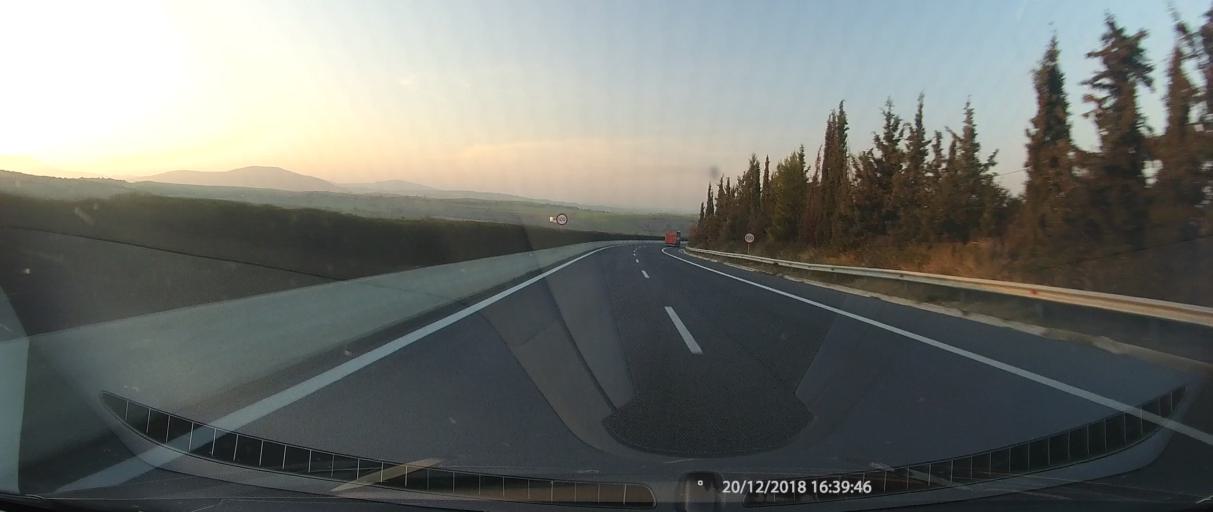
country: GR
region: Thessaly
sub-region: Nomos Magnisias
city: Velestino
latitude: 39.3638
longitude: 22.7712
